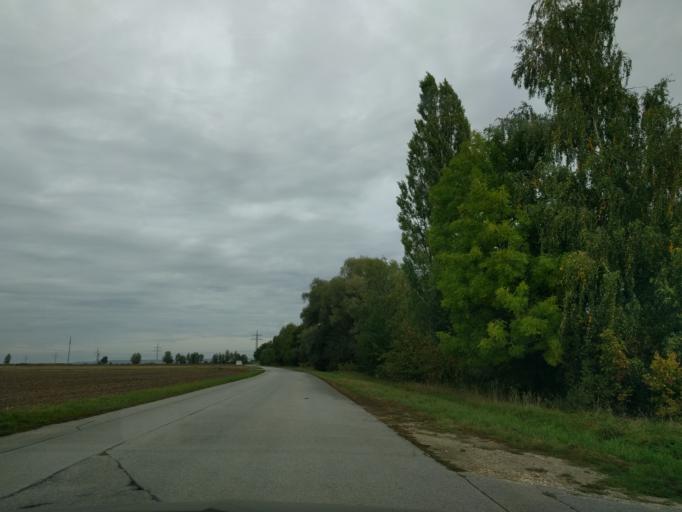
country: DE
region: Bavaria
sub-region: Lower Bavaria
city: Otzing
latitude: 48.7706
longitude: 12.8387
